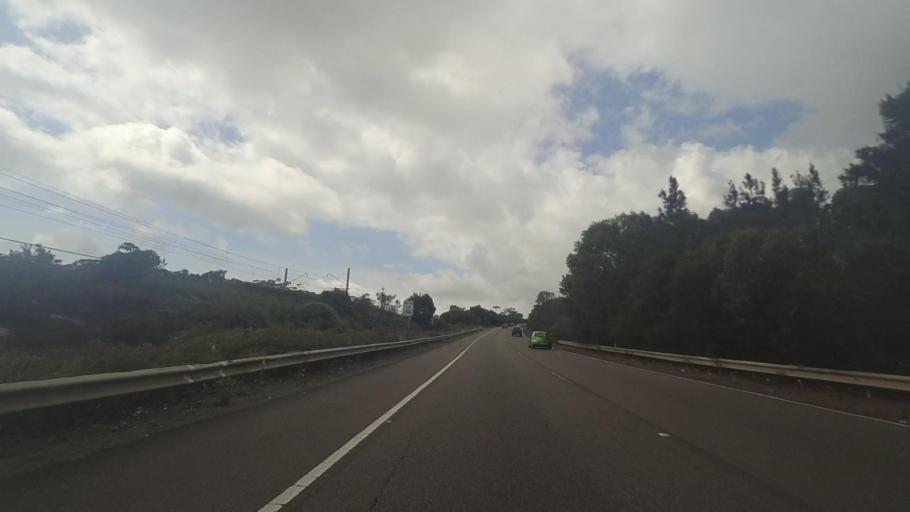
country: AU
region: New South Wales
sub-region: Sutherland Shire
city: Heathcote
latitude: -34.1091
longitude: 150.9936
